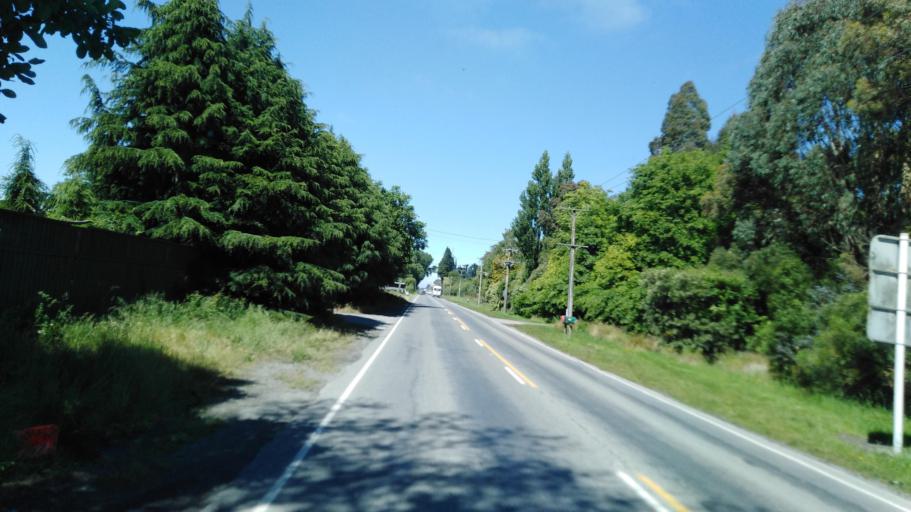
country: NZ
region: Canterbury
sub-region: Selwyn District
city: Prebbleton
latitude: -43.5209
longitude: 172.5041
